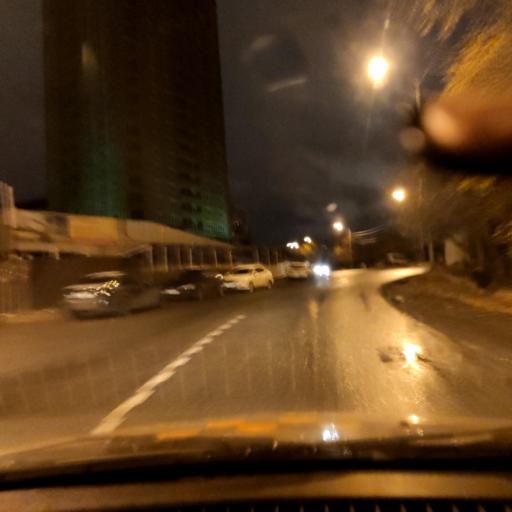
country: RU
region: Bashkortostan
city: Ufa
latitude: 54.7502
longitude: 55.9653
